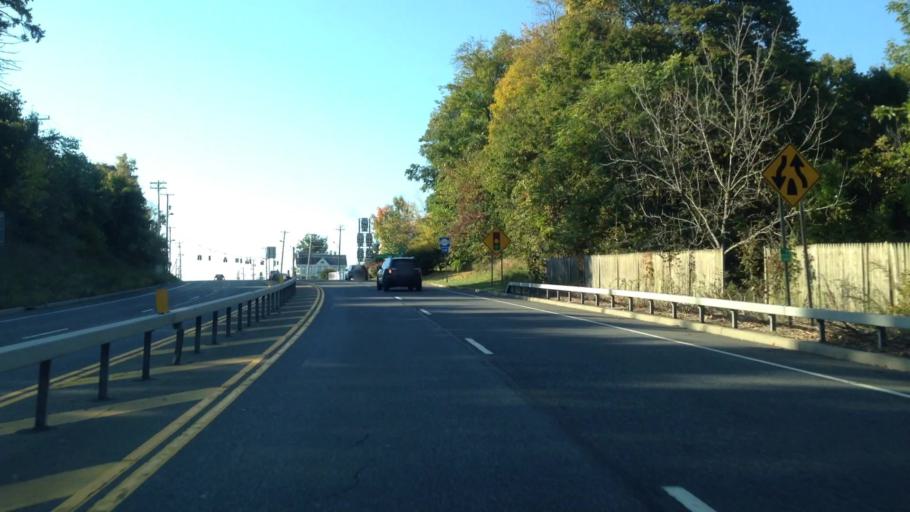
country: US
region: New York
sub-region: Ulster County
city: Highland
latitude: 41.7185
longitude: -73.9622
